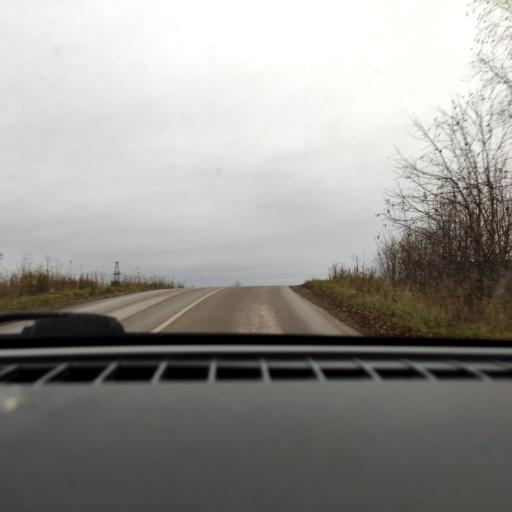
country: RU
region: Perm
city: Ferma
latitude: 57.9259
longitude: 56.3319
